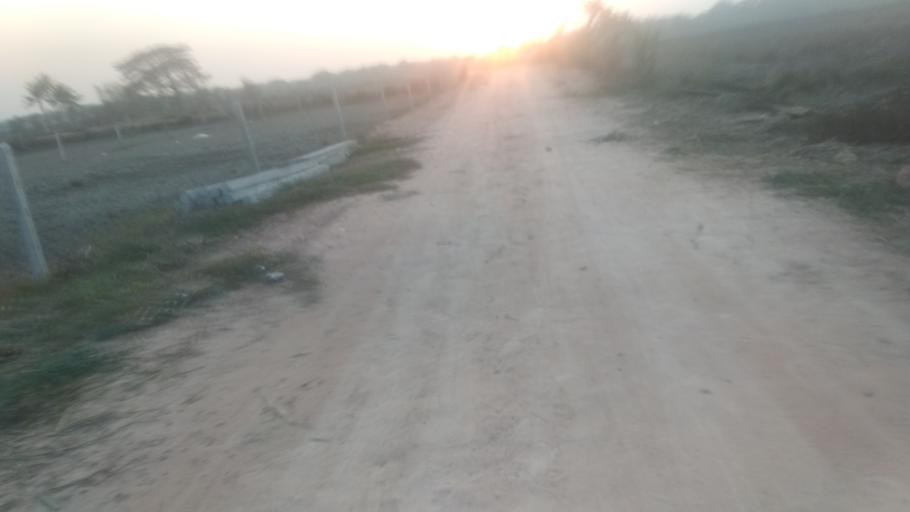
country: MM
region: Yangon
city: Kanbe
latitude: 16.8801
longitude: 95.9796
